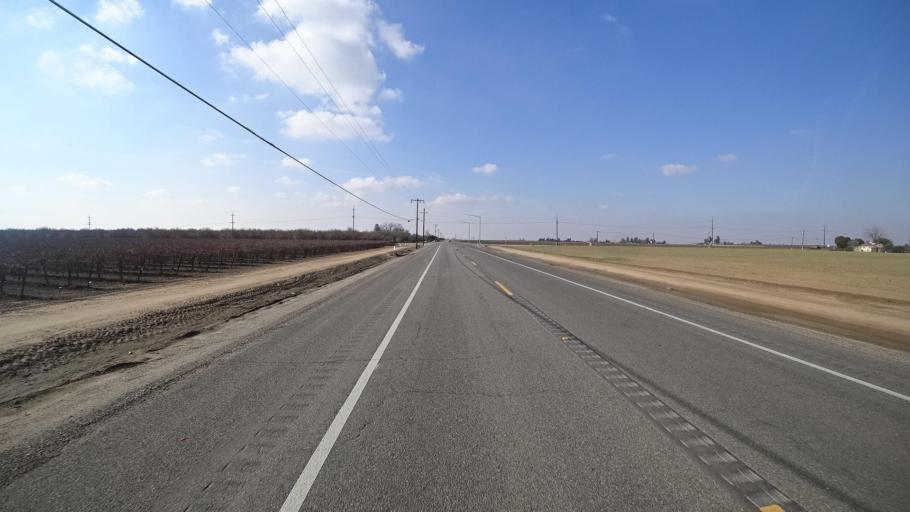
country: US
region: California
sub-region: Kern County
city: Arvin
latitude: 35.2088
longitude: -118.8763
